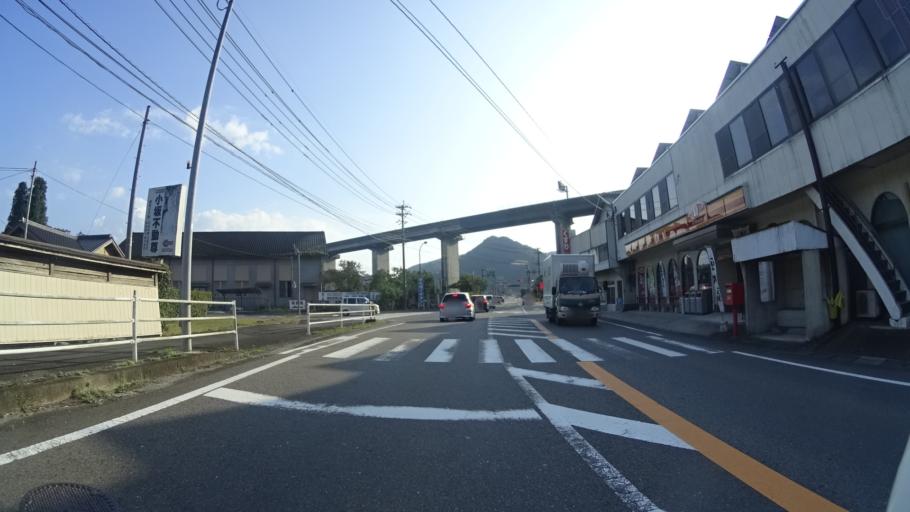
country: JP
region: Oita
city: Bungo-Takada-shi
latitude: 33.4791
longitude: 131.3337
